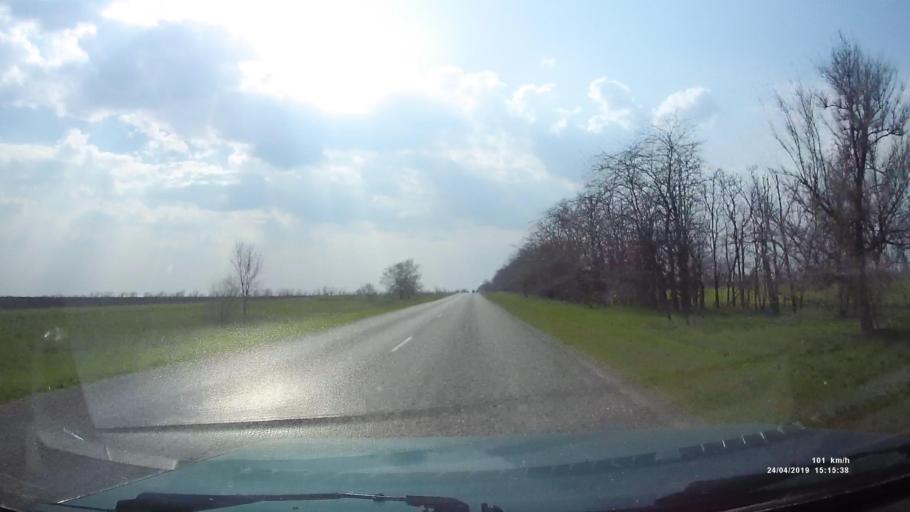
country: RU
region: Rostov
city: Remontnoye
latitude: 46.5465
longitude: 43.2309
